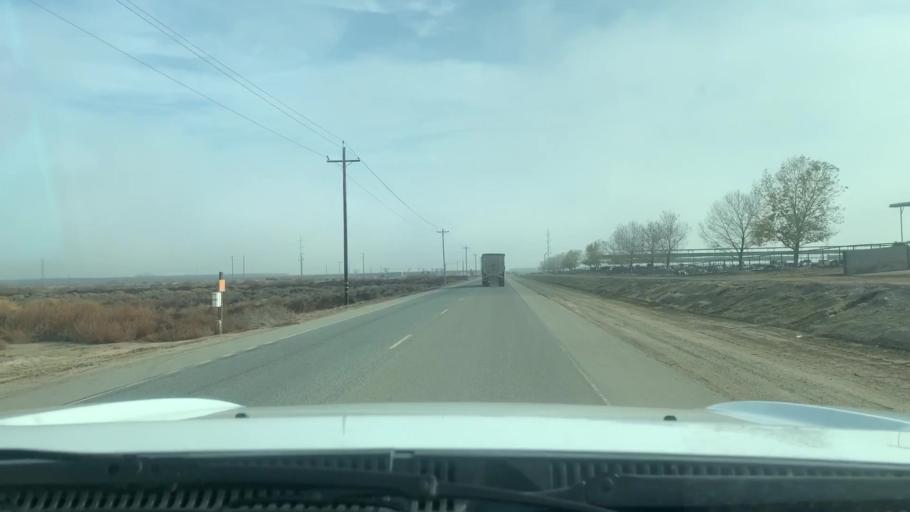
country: US
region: California
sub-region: Kern County
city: Buttonwillow
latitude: 35.5005
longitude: -119.4544
